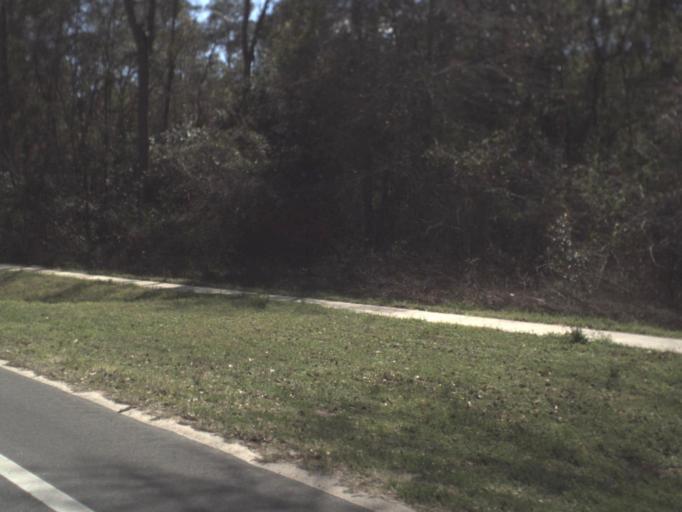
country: US
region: Florida
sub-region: Gadsden County
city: Gretna
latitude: 30.6147
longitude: -84.6614
